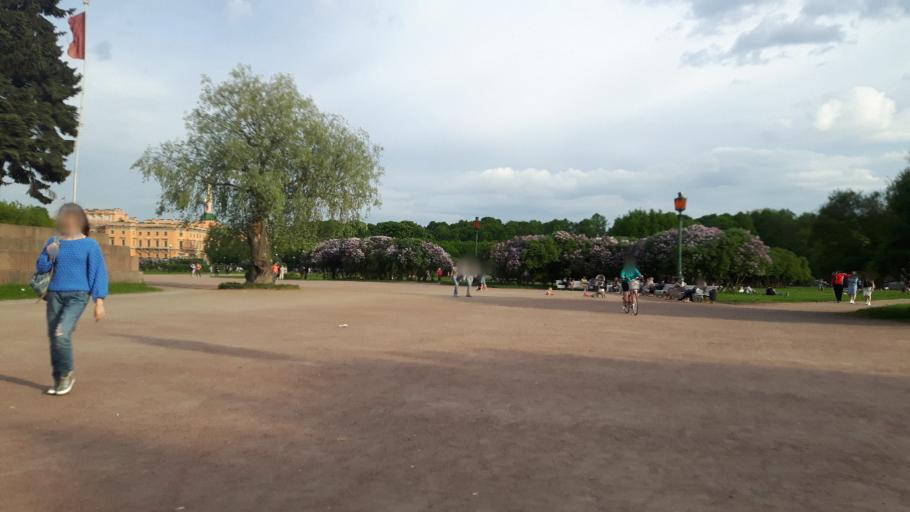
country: RU
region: St.-Petersburg
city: Saint Petersburg
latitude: 59.9436
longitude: 30.3310
